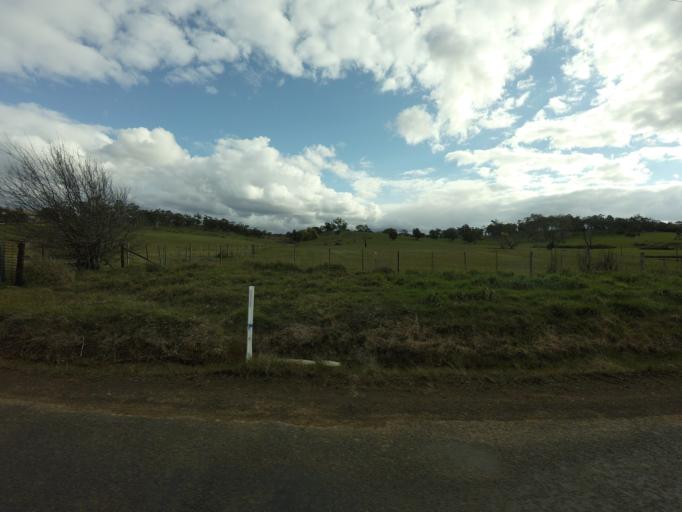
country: AU
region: Tasmania
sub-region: Northern Midlands
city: Evandale
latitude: -41.8780
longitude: 147.3054
